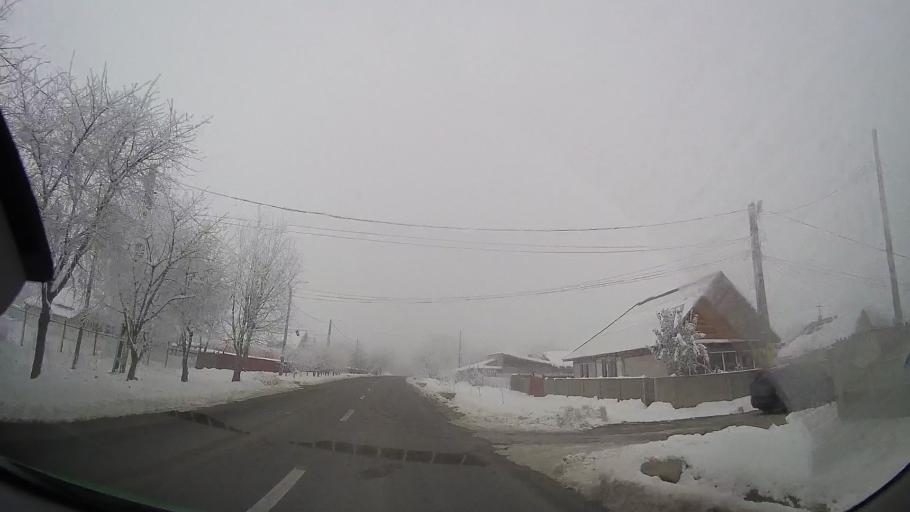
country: RO
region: Iasi
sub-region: Comuna Mogosesti-Siret
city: Mogosesti-Siret
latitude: 47.1620
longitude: 26.7723
